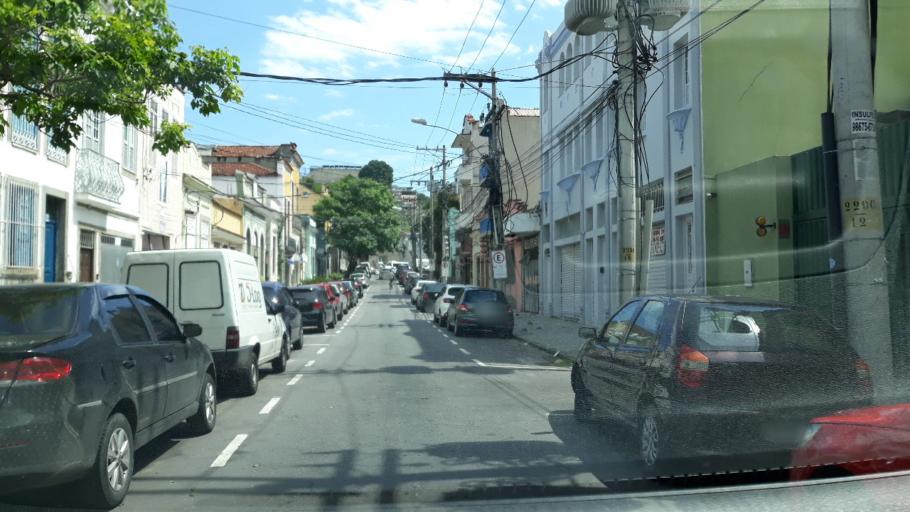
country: BR
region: Rio de Janeiro
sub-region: Rio De Janeiro
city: Rio de Janeiro
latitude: -22.9120
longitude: -43.2027
